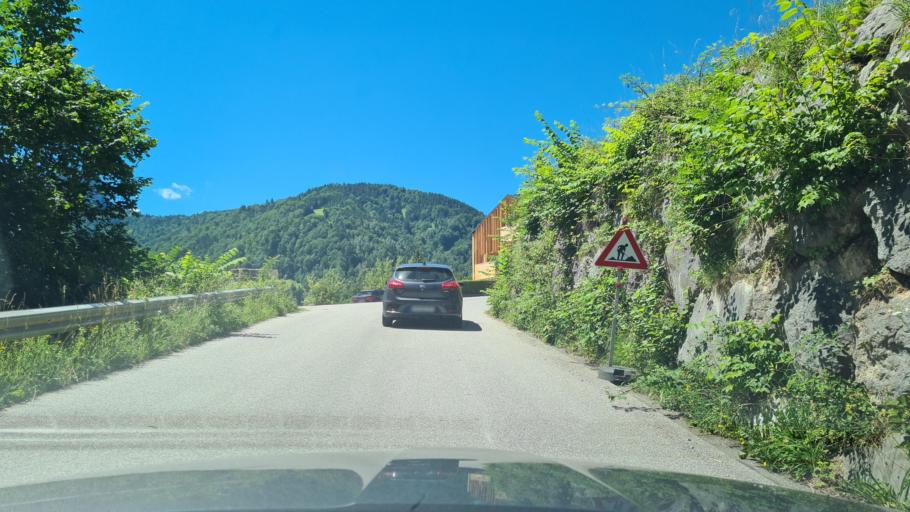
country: AT
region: Salzburg
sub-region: Politischer Bezirk Zell am See
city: Unken
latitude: 47.6476
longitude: 12.6952
